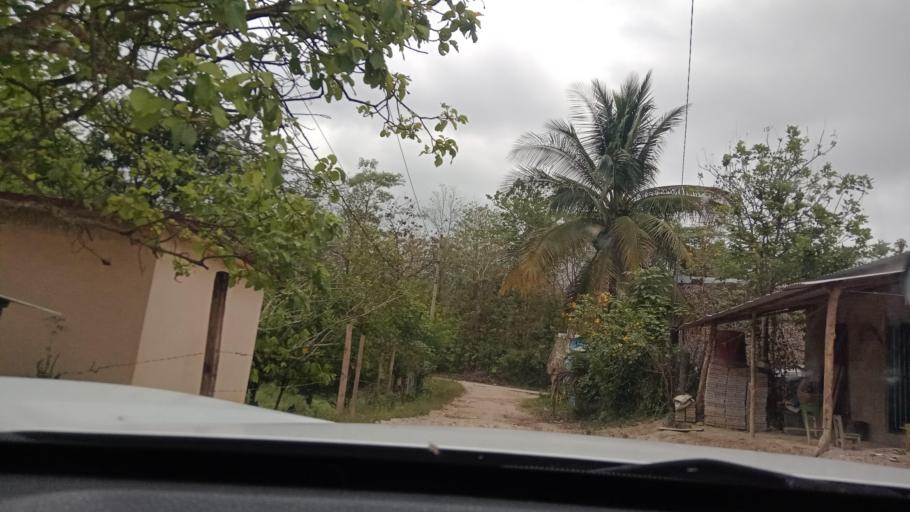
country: MX
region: Tabasco
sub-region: Huimanguillo
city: Francisco Rueda
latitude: 17.5878
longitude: -94.0918
